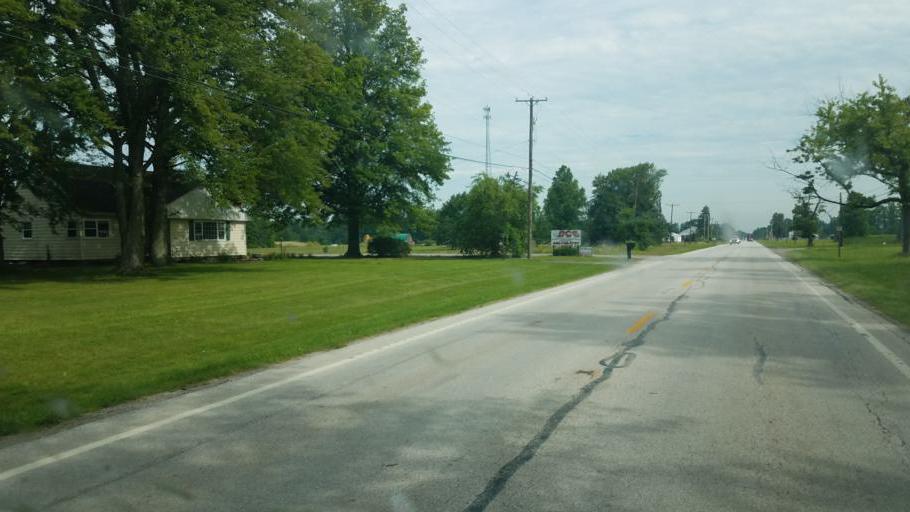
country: US
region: Ohio
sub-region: Lorain County
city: Eaton Estates
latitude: 41.3003
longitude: -82.0208
